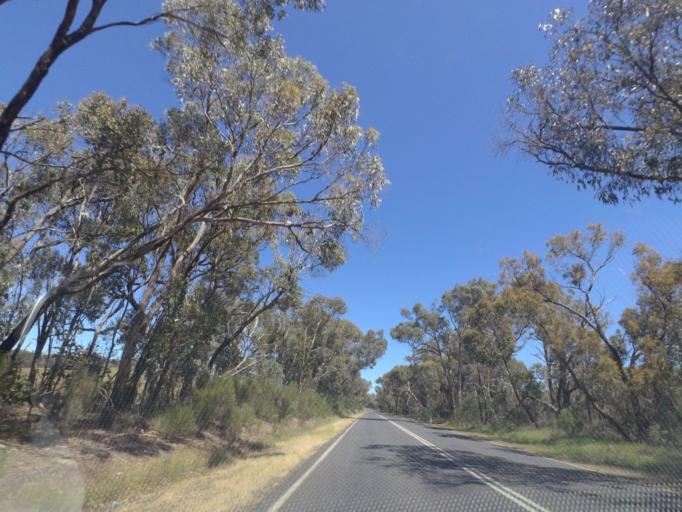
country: AU
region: Victoria
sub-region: Hume
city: Sunbury
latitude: -37.3029
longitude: 144.8639
